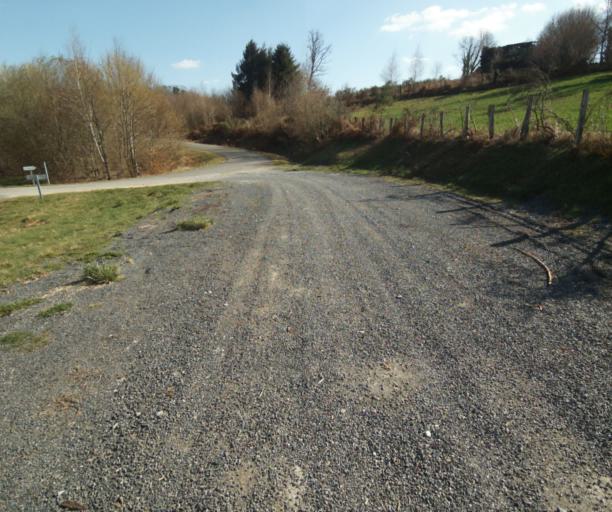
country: FR
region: Limousin
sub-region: Departement de la Correze
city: Saint-Mexant
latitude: 45.2870
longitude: 1.6178
